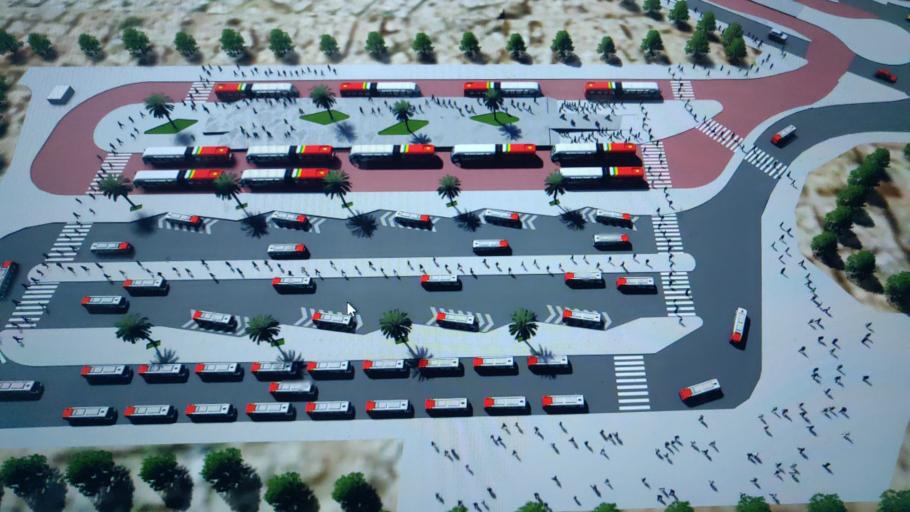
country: SN
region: Dakar
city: Grand Dakar
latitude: 14.7222
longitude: -17.4374
